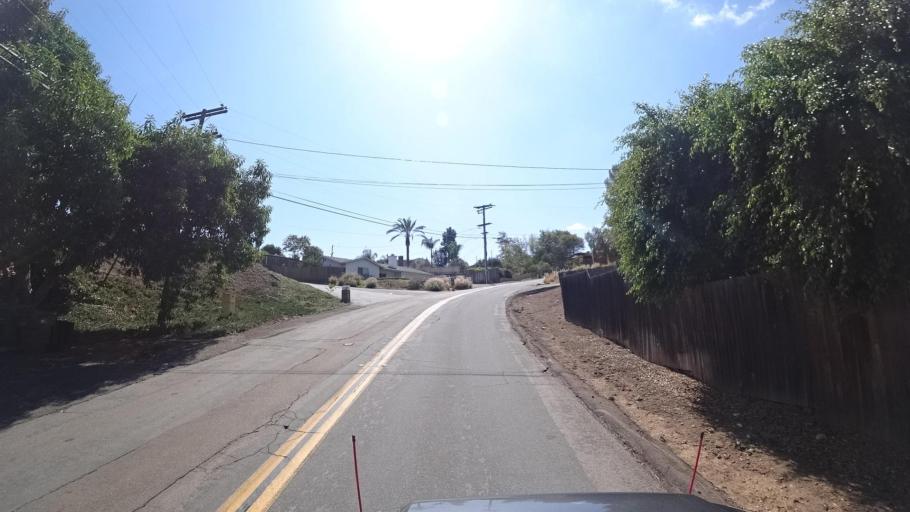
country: US
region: California
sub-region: San Diego County
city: Spring Valley
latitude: 32.7431
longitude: -116.9839
